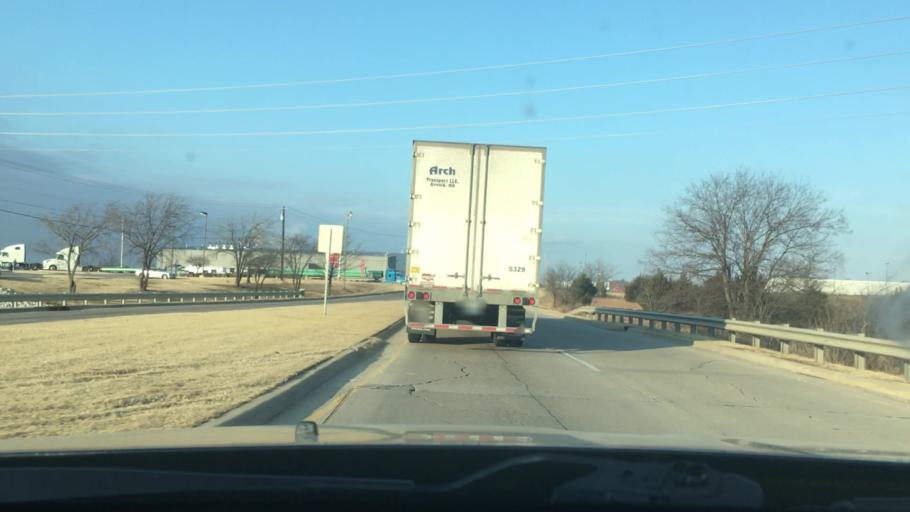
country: US
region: Oklahoma
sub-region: Carter County
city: Ardmore
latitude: 34.2021
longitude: -97.1665
